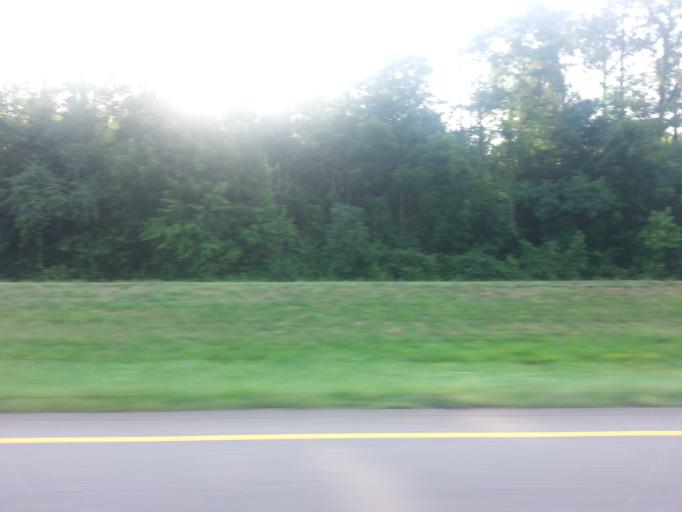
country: US
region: Tennessee
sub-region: Loudon County
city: Lenoir City
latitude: 35.8596
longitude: -84.2594
